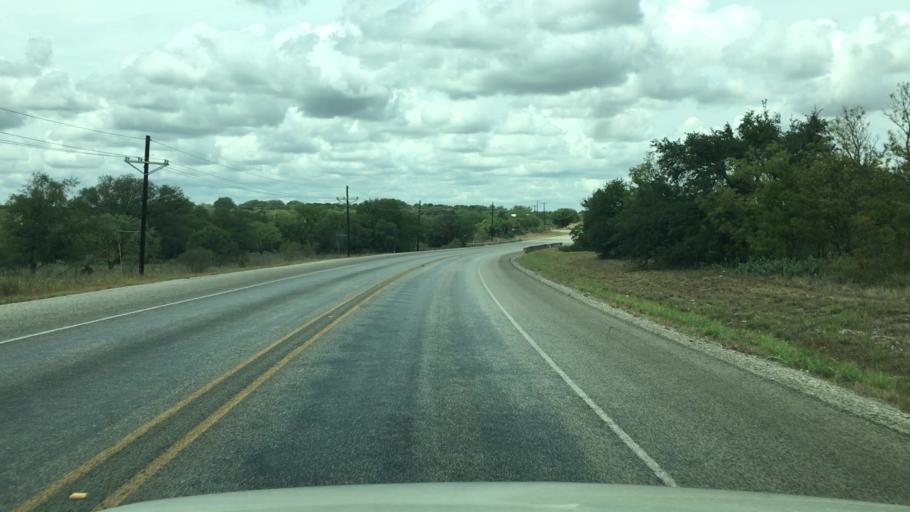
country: US
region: Texas
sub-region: McCulloch County
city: Brady
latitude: 31.0047
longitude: -99.2009
